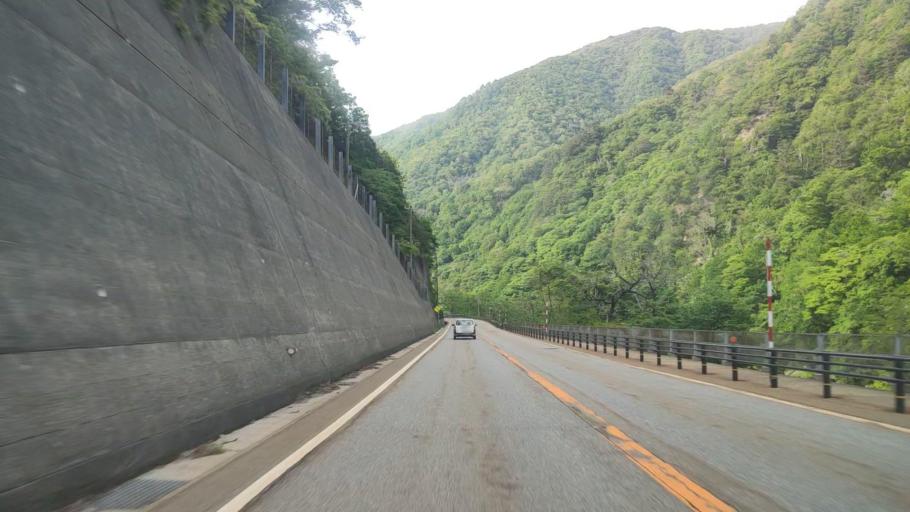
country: JP
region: Gifu
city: Takayama
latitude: 36.3564
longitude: 137.2882
